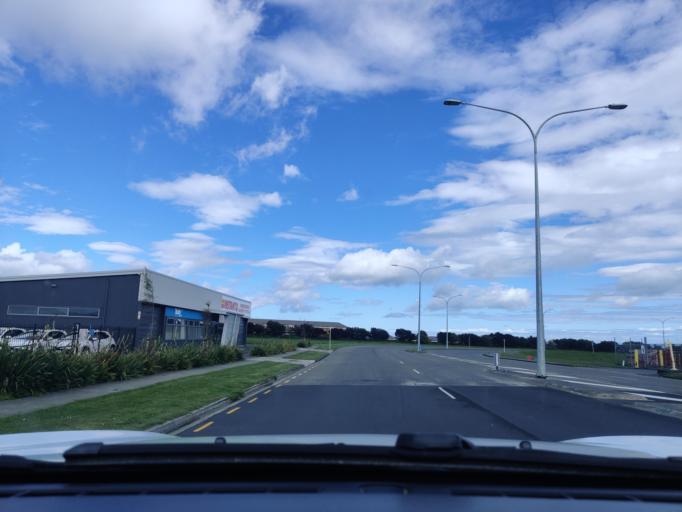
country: NZ
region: Manawatu-Wanganui
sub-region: Palmerston North City
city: Palmerston North
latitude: -40.3266
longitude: 175.6192
